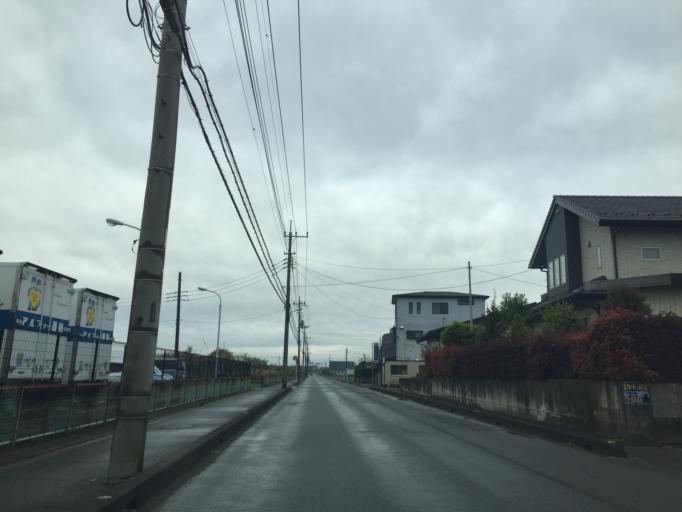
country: JP
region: Saitama
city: Kamifukuoka
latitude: 35.8805
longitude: 139.5610
